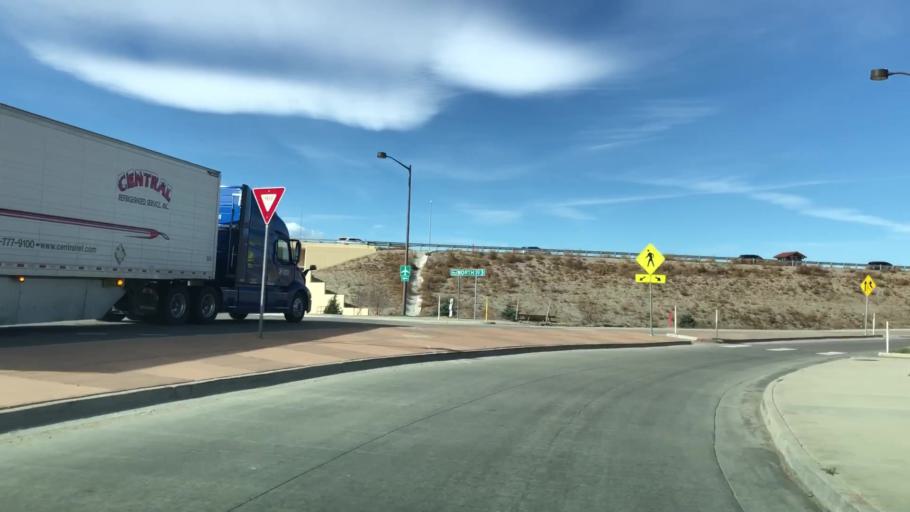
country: US
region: Colorado
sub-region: Larimer County
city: Loveland
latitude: 40.4361
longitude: -104.9909
